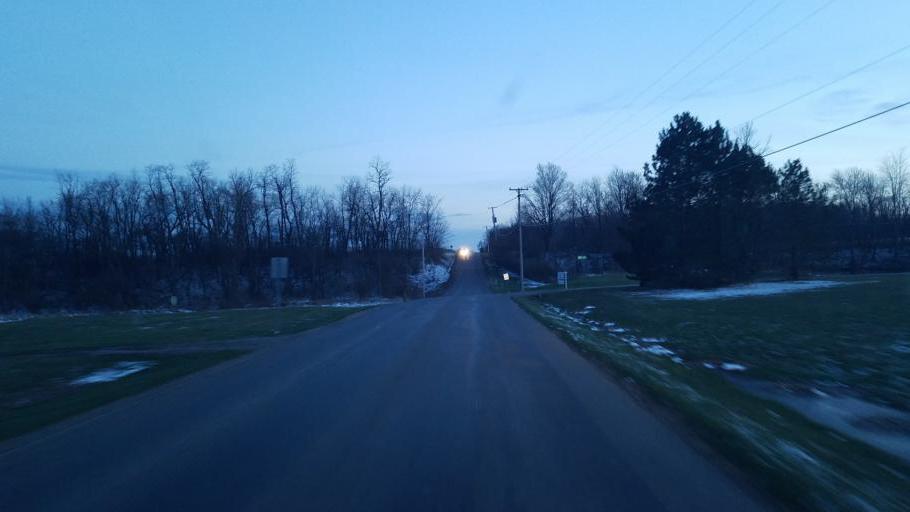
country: US
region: Ohio
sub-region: Ashland County
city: Ashland
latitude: 40.8414
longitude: -82.2795
